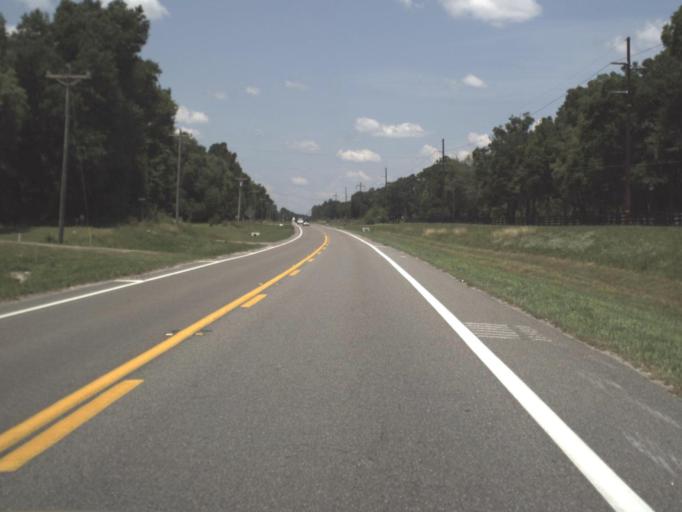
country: US
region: Florida
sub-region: Union County
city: Lake Butler
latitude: 30.0006
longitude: -82.2779
